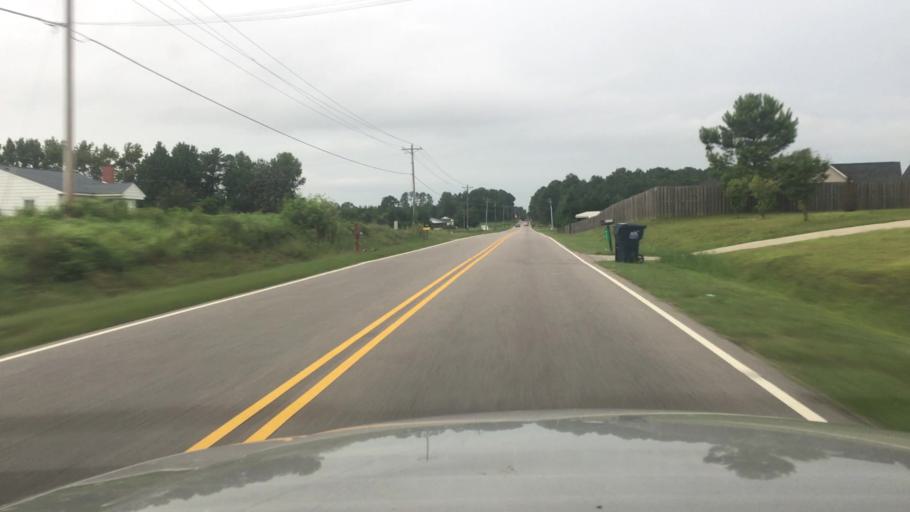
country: US
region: North Carolina
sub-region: Hoke County
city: Rockfish
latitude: 34.9708
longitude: -79.0543
